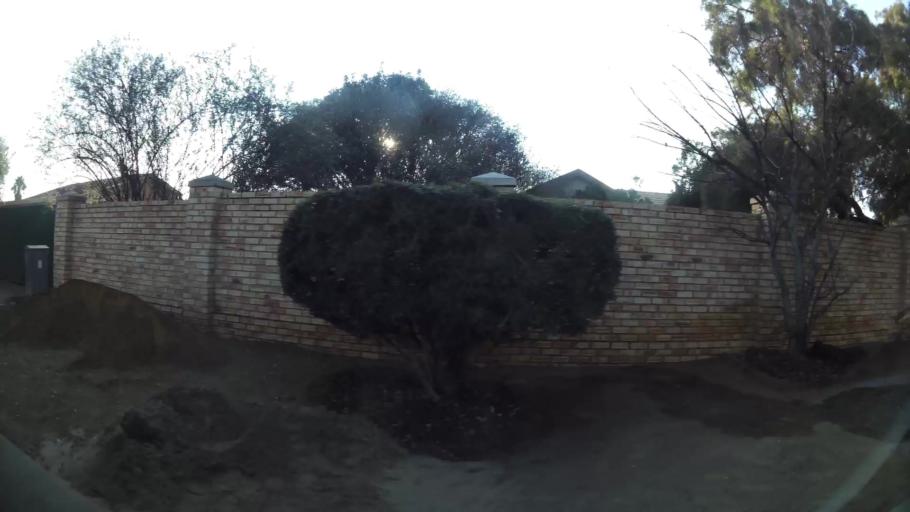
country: ZA
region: Orange Free State
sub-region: Mangaung Metropolitan Municipality
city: Bloemfontein
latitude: -29.1494
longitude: 26.1674
